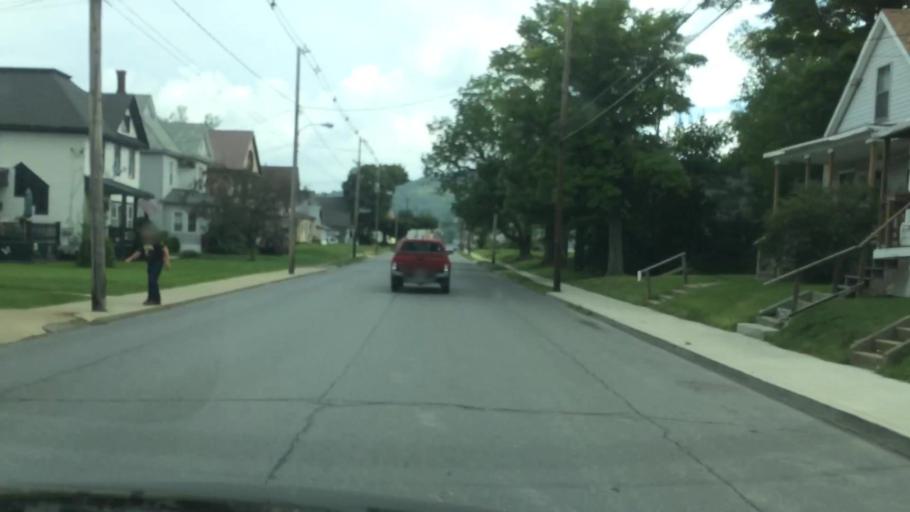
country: US
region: Pennsylvania
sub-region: McKean County
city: Bradford
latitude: 41.9624
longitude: -78.6316
